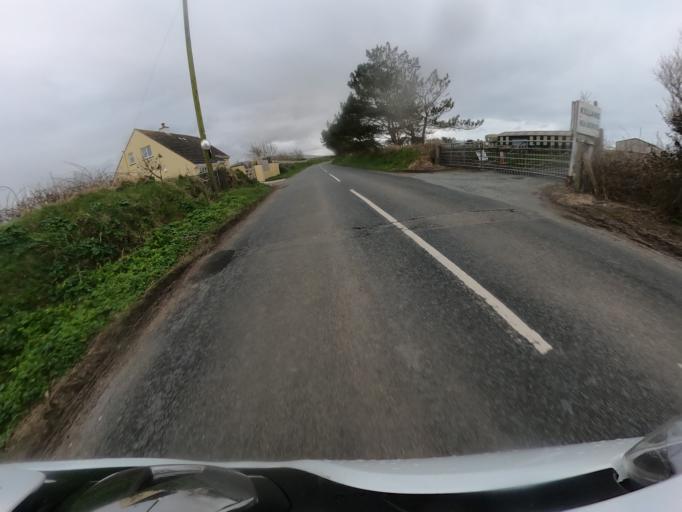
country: IM
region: Ramsey
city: Ramsey
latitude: 54.3366
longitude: -4.5518
